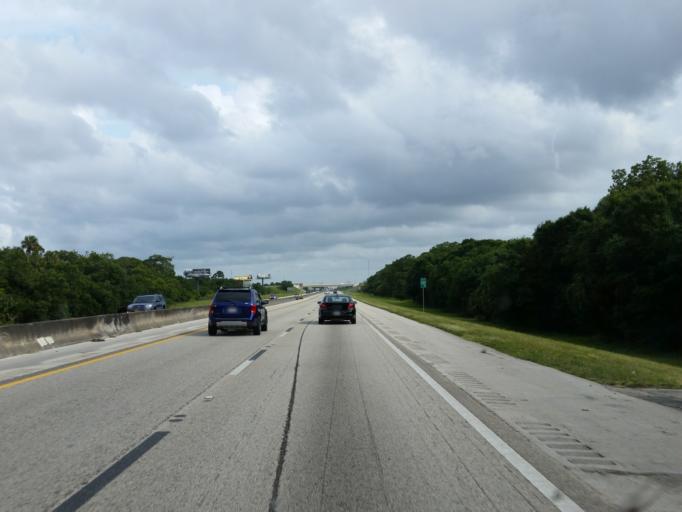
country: US
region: Florida
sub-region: Saint Lucie County
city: Fort Pierce South
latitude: 27.4021
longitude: -80.3977
